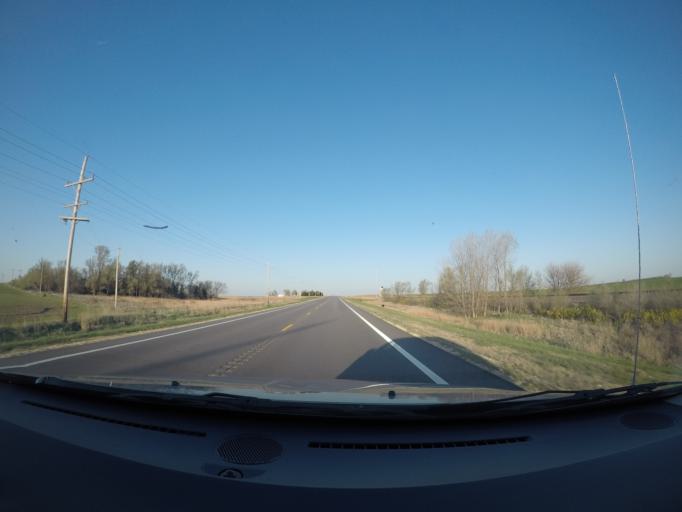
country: US
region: Kansas
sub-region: Stafford County
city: Stafford
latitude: 37.8271
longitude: -98.3895
